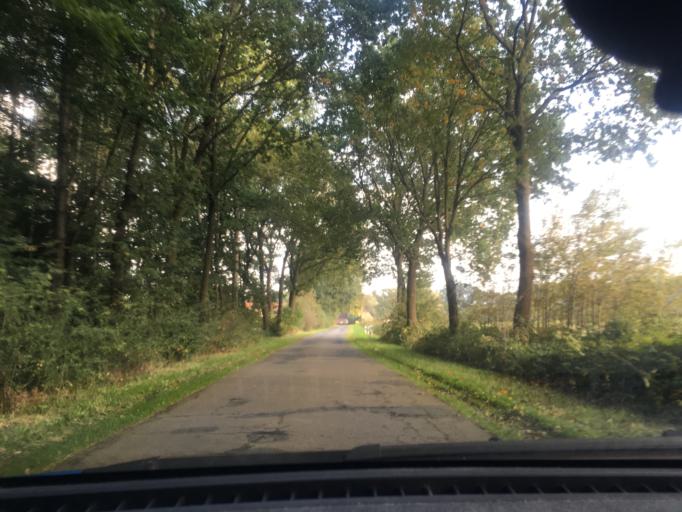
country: DE
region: Lower Saxony
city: Vastorf
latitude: 53.2036
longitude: 10.5740
